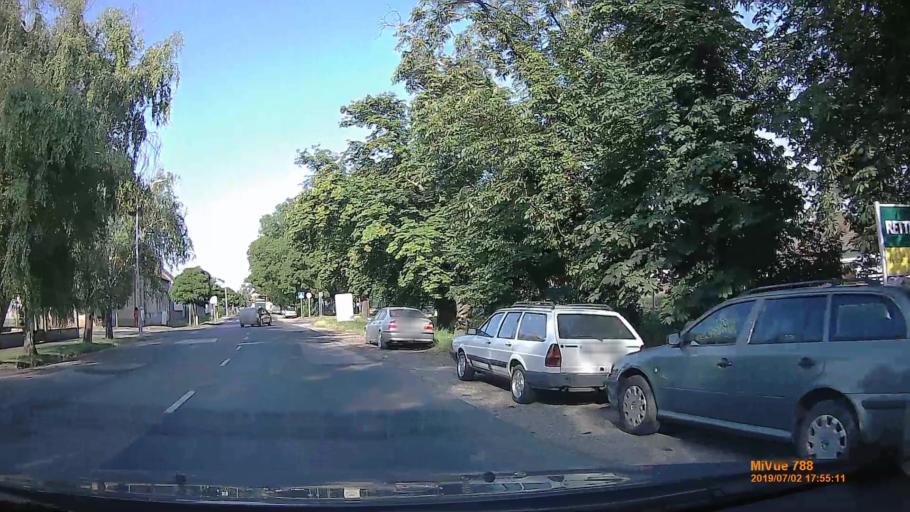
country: HU
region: Gyor-Moson-Sopron
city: Mosonmagyarovar
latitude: 47.8512
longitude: 17.2690
